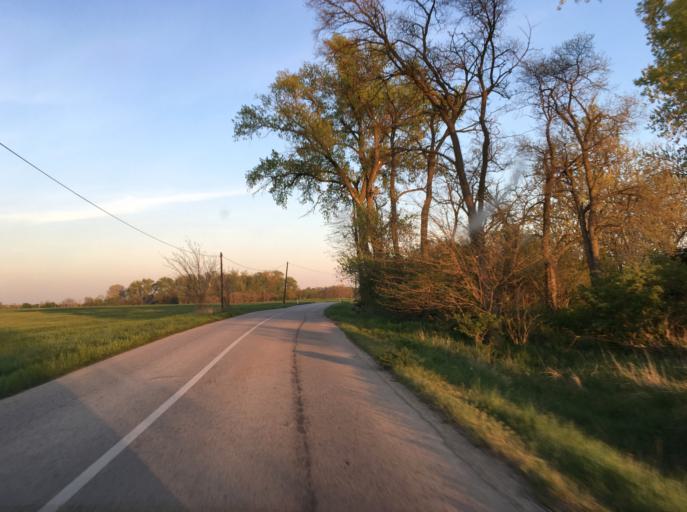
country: SK
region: Nitriansky
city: Kolarovo
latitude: 47.8830
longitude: 17.9061
